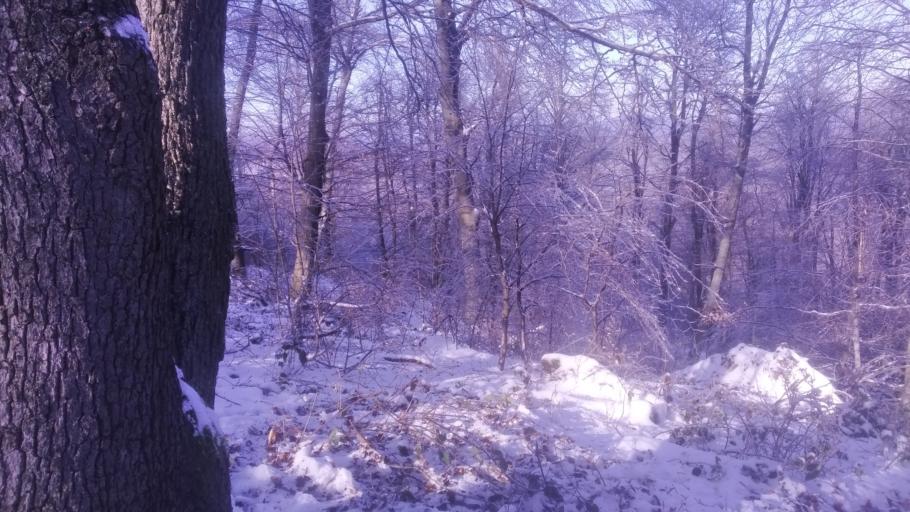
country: HU
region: Pest
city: Csobanka
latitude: 47.6928
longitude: 18.9665
